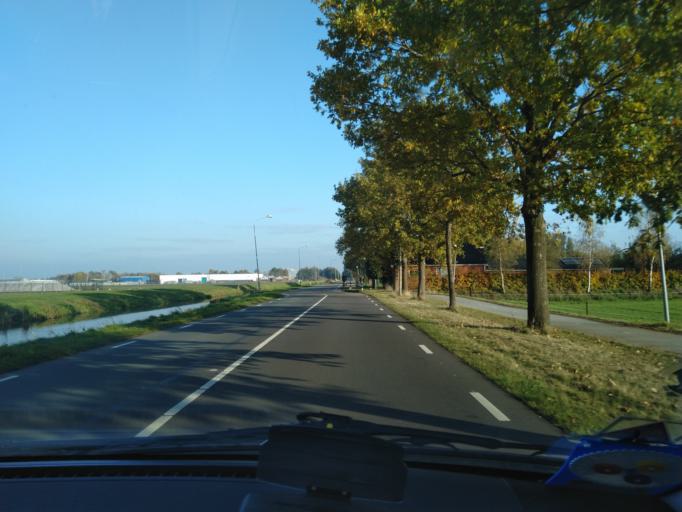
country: NL
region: Groningen
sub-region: Gemeente Hoogezand-Sappemeer
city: Sappemeer
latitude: 53.1548
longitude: 6.7998
